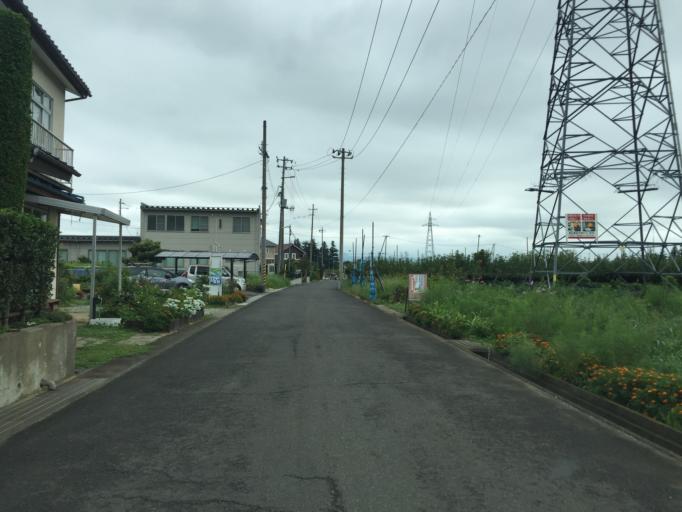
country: JP
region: Fukushima
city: Fukushima-shi
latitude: 37.7675
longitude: 140.4000
